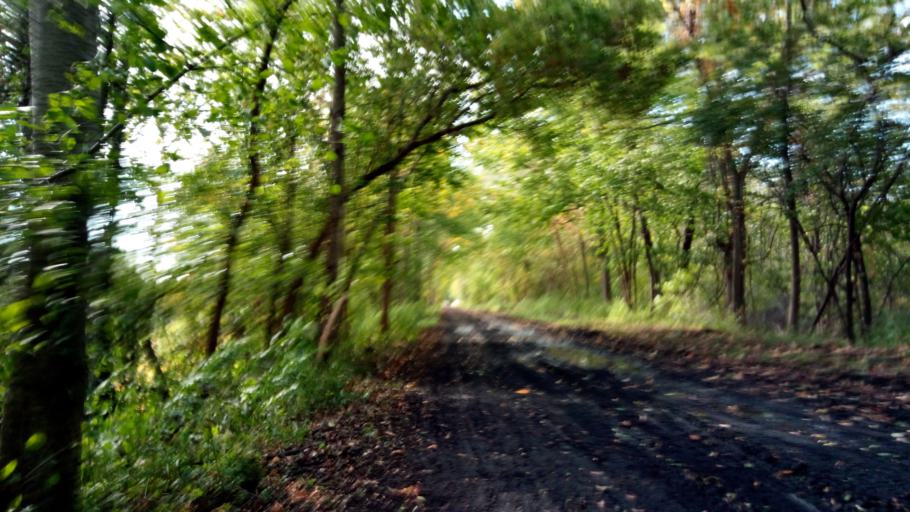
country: US
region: New York
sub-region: Wayne County
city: Clyde
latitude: 43.0653
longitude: -76.8365
